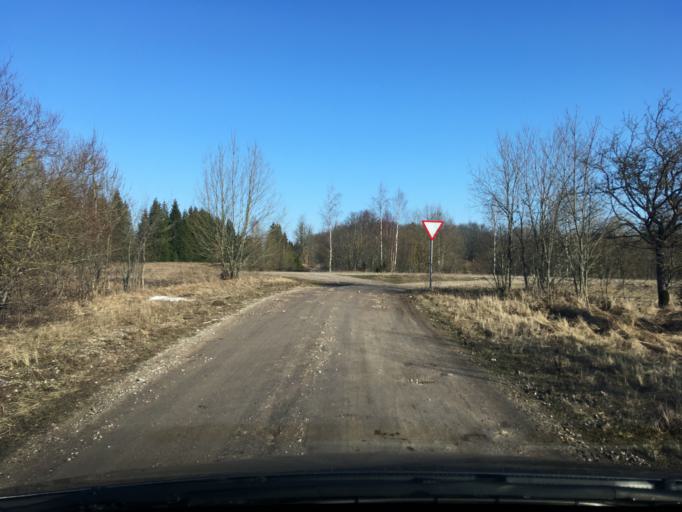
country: EE
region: Laeaene
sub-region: Lihula vald
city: Lihula
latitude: 58.6333
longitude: 23.6892
